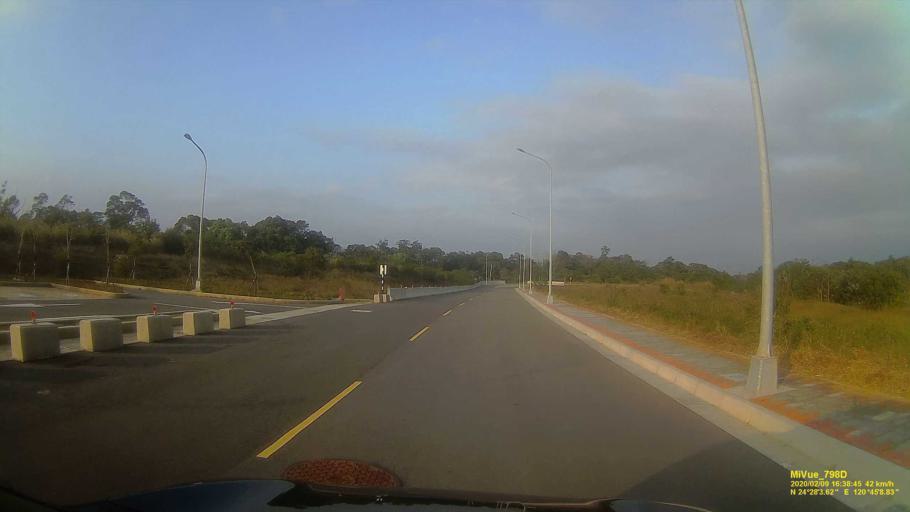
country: TW
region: Taiwan
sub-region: Miaoli
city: Miaoli
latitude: 24.4679
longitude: 120.7525
